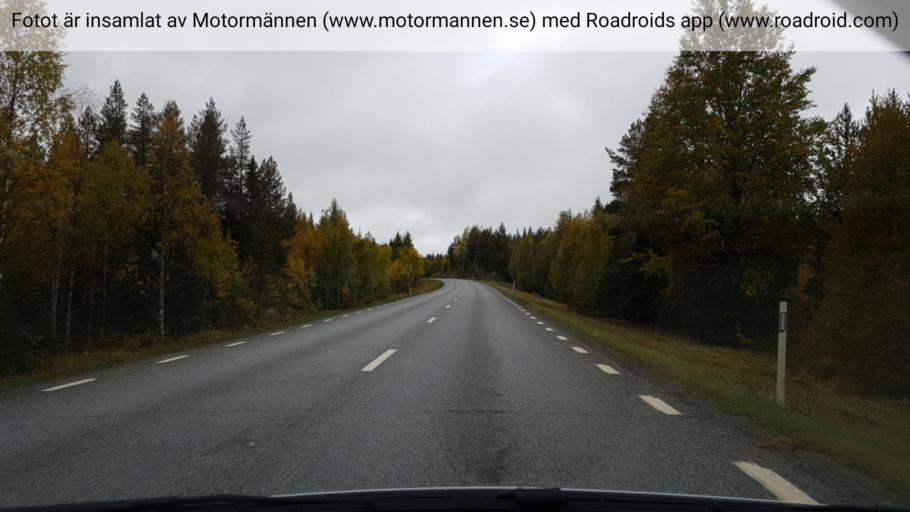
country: SE
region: Jaemtland
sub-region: OEstersunds Kommun
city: Lit
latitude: 63.4061
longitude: 15.0622
